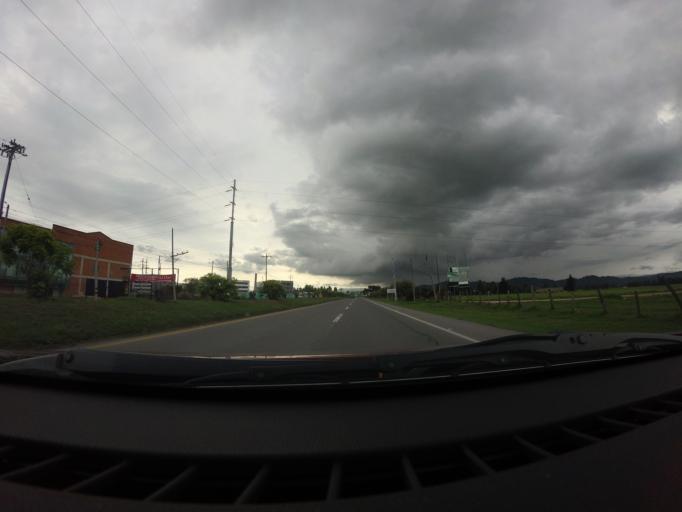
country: CO
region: Cundinamarca
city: Funza
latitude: 4.7767
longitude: -74.1801
